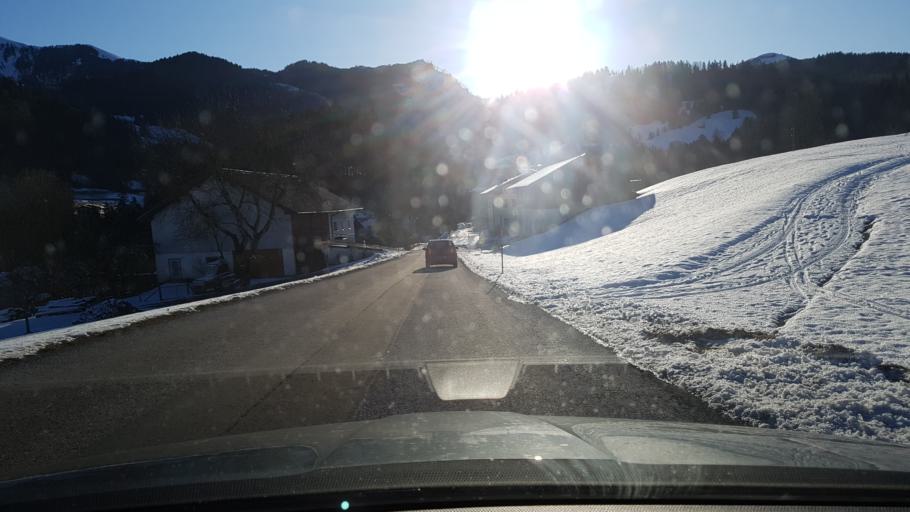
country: AT
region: Salzburg
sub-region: Politischer Bezirk Hallein
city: Scheffau am Tennengebirge
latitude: 47.6512
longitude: 13.2149
